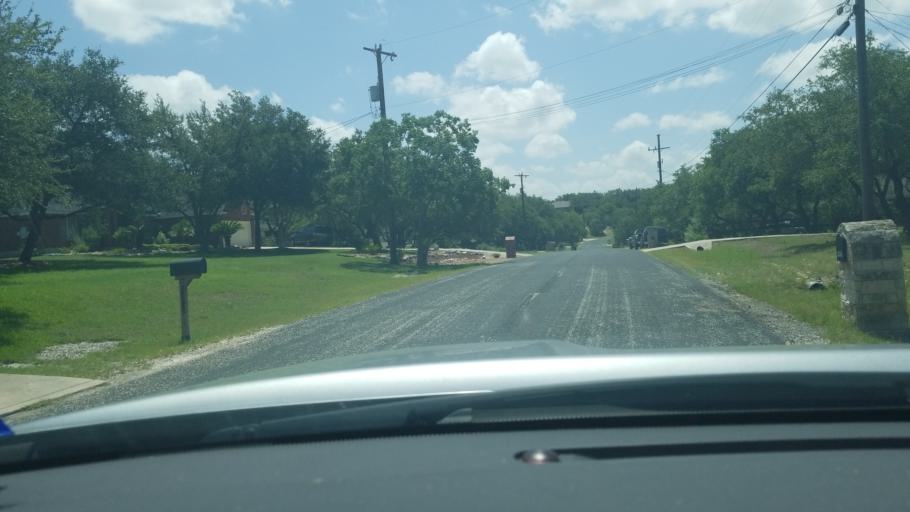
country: US
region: Texas
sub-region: Bexar County
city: Timberwood Park
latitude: 29.6916
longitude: -98.4873
